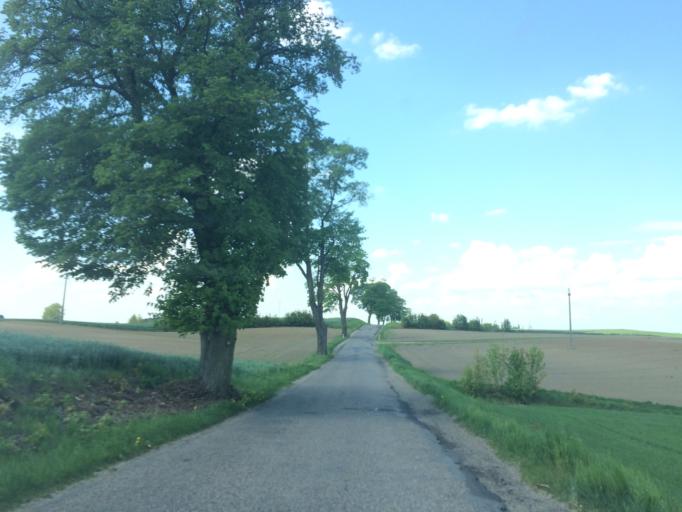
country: PL
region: Warmian-Masurian Voivodeship
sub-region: Powiat ilawski
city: Lubawa
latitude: 53.4087
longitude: 19.7870
